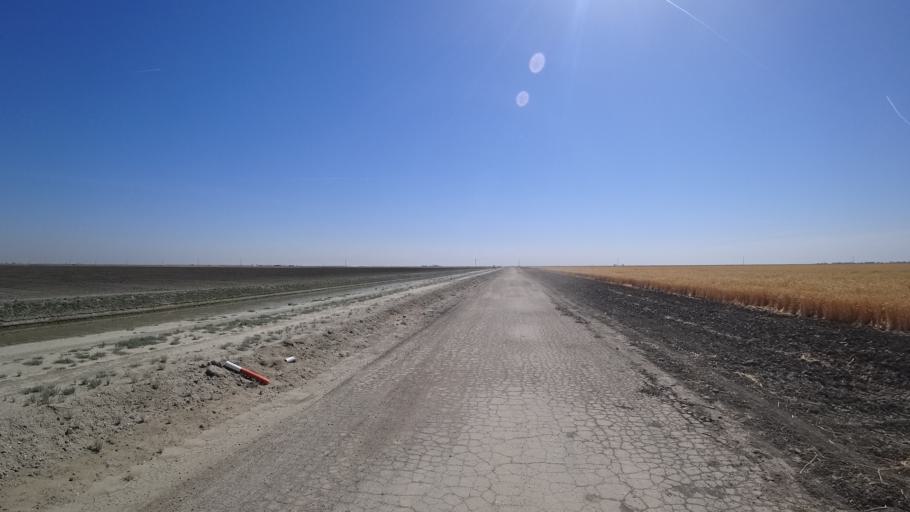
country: US
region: California
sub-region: Tulare County
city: Alpaugh
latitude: 35.9781
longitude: -119.5408
